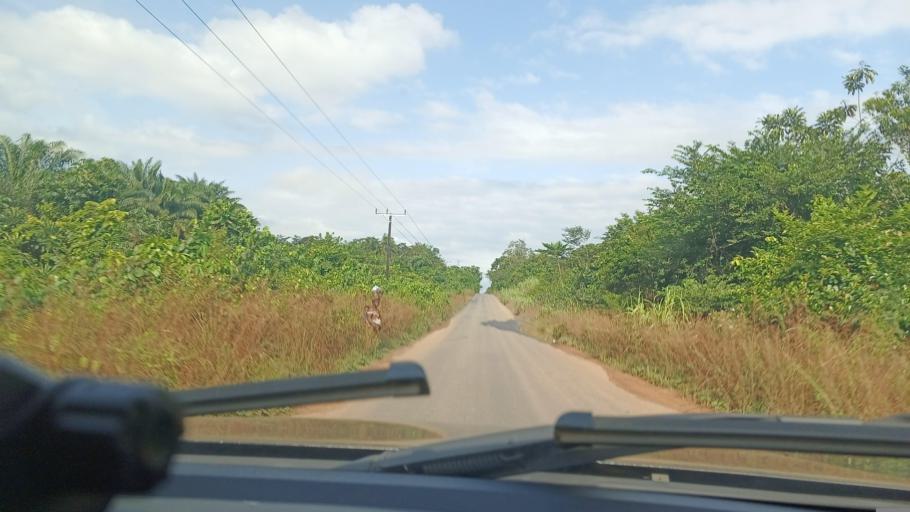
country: LR
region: Bomi
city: Tubmanburg
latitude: 6.6930
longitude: -10.8940
